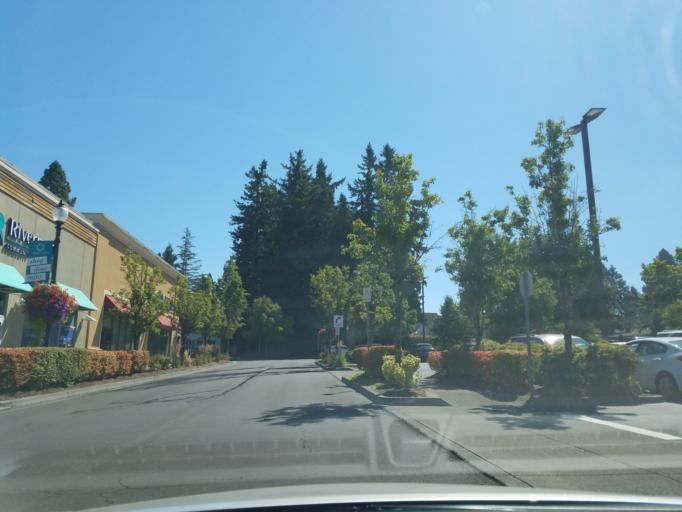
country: US
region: Oregon
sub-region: Multnomah County
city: Gresham
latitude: 45.5052
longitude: -122.4395
